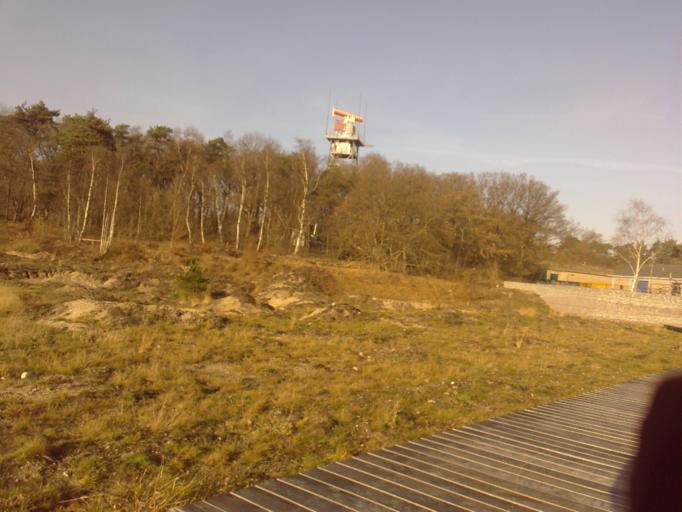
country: NL
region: Utrecht
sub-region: Gemeente Soest
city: Soest
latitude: 52.1345
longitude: 5.2768
